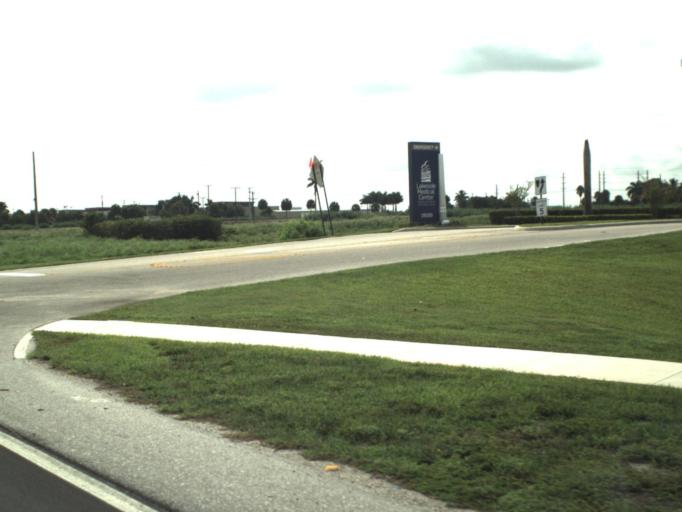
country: US
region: Florida
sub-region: Palm Beach County
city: Belle Glade
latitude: 26.7257
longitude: -80.6703
